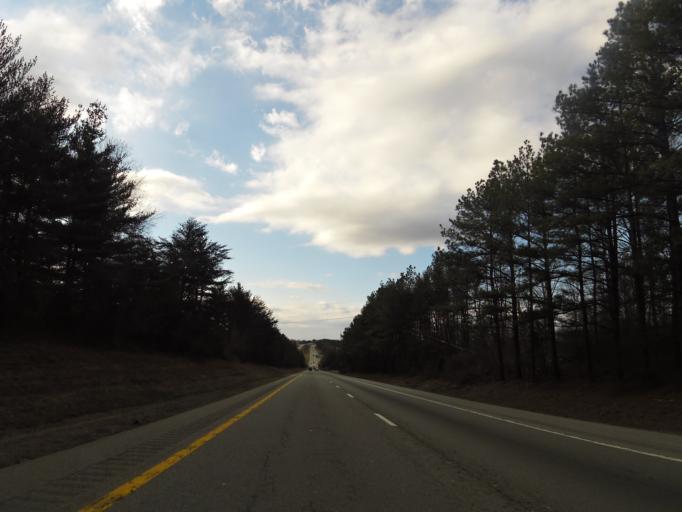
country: US
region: Tennessee
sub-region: Cumberland County
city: Fairfield Glade
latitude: 35.9222
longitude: -84.9088
